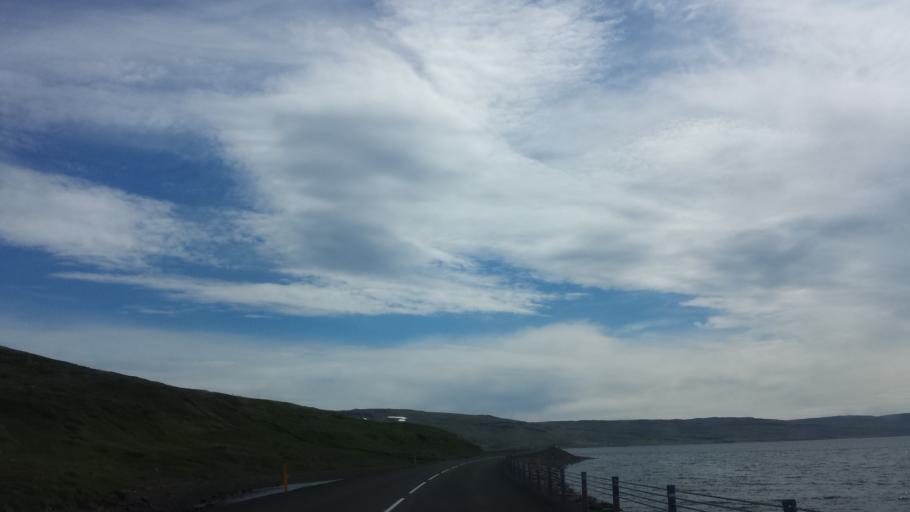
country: IS
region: West
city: Stykkisholmur
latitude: 65.7717
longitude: -21.7637
